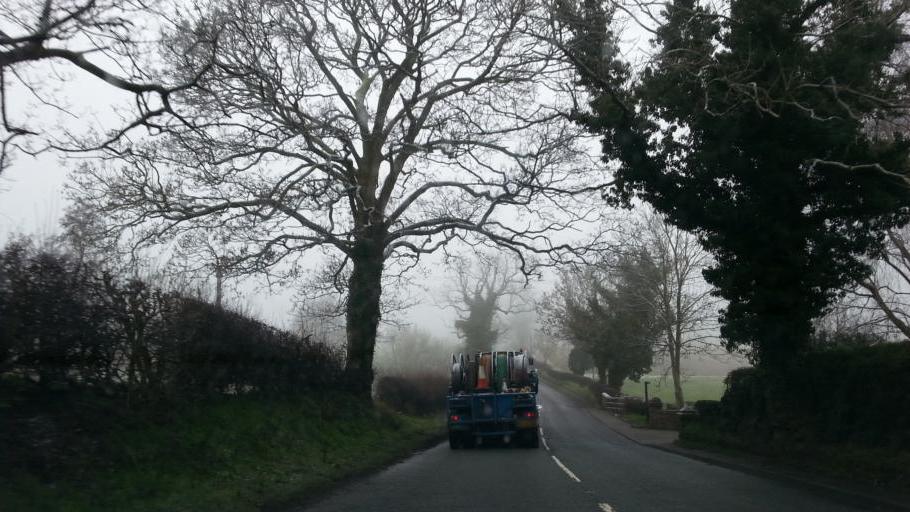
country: GB
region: England
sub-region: Cheshire East
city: Siddington
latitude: 53.2056
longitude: -2.2254
